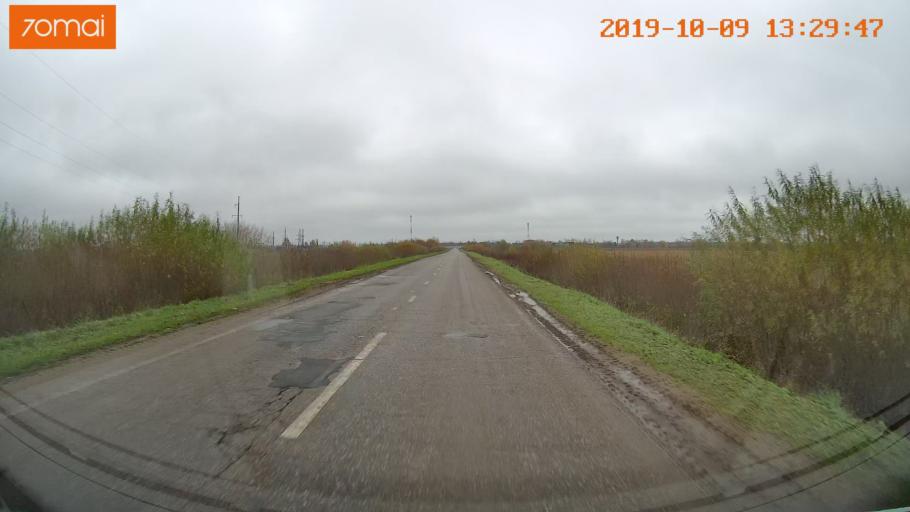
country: RU
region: Jaroslavl
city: Lyubim
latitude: 58.3182
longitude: 40.9955
